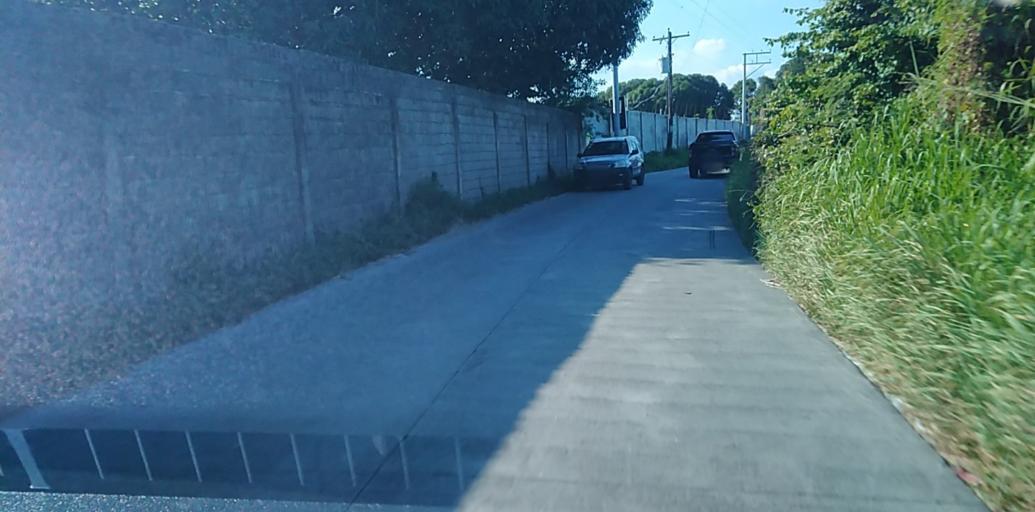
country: PH
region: Central Luzon
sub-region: Province of Pampanga
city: Acli
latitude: 15.1108
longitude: 120.6499
